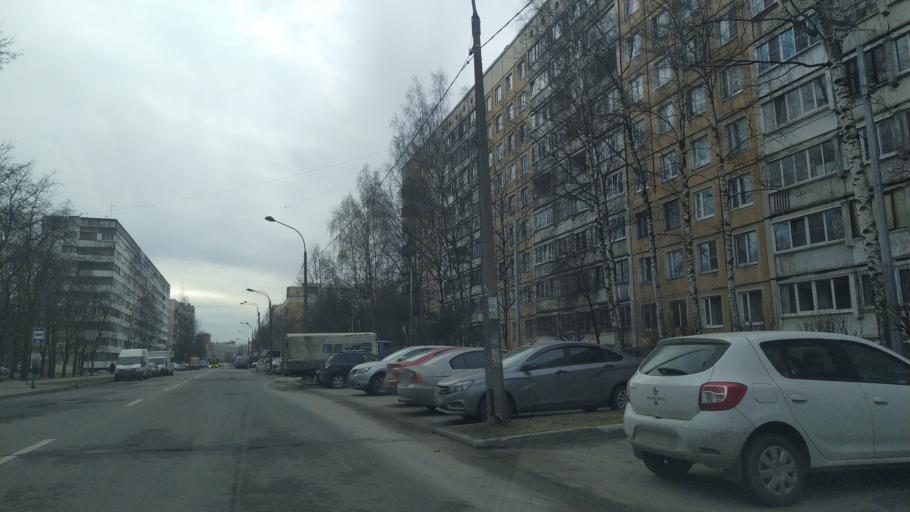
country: RU
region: St.-Petersburg
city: Grazhdanka
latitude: 60.0279
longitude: 30.4242
